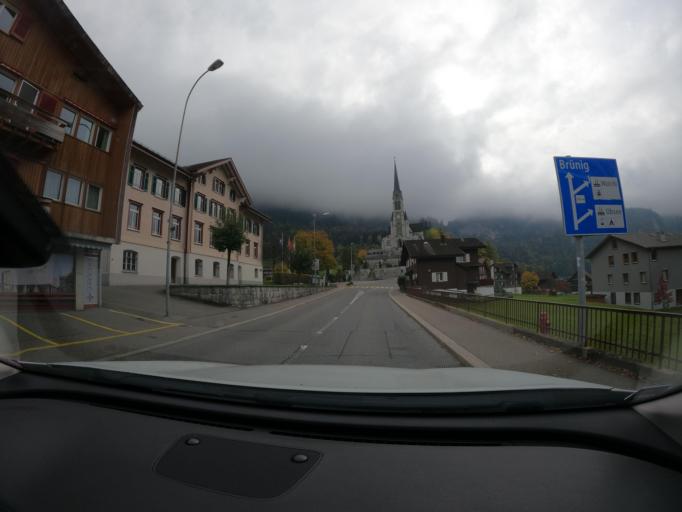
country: CH
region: Obwalden
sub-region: Obwalden
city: Lungern
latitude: 46.7840
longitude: 8.1591
